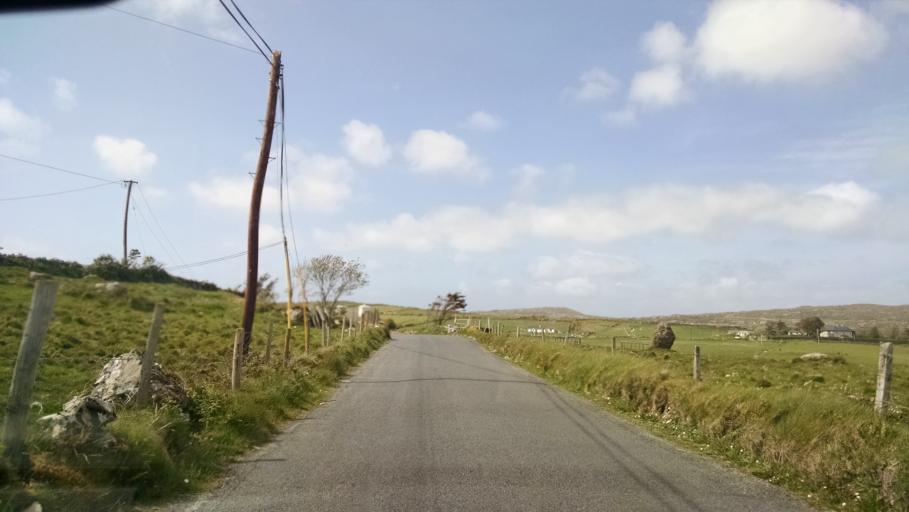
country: IE
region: Connaught
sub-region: County Galway
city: Clifden
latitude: 53.5105
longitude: -10.0999
